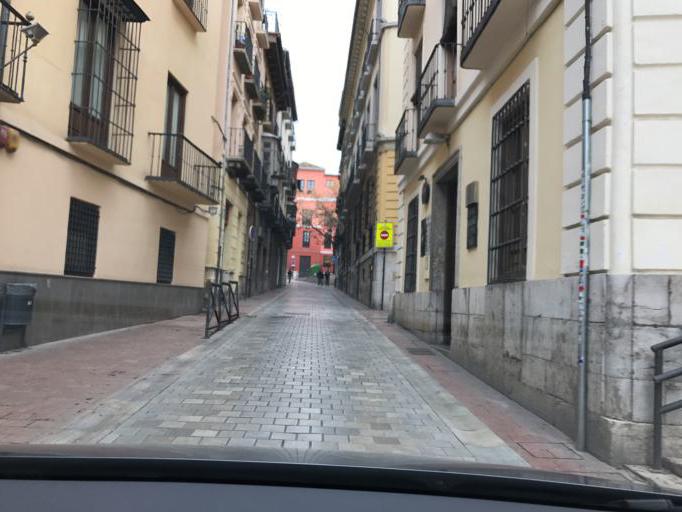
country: ES
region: Andalusia
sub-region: Provincia de Granada
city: Granada
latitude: 37.1736
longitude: -3.5968
